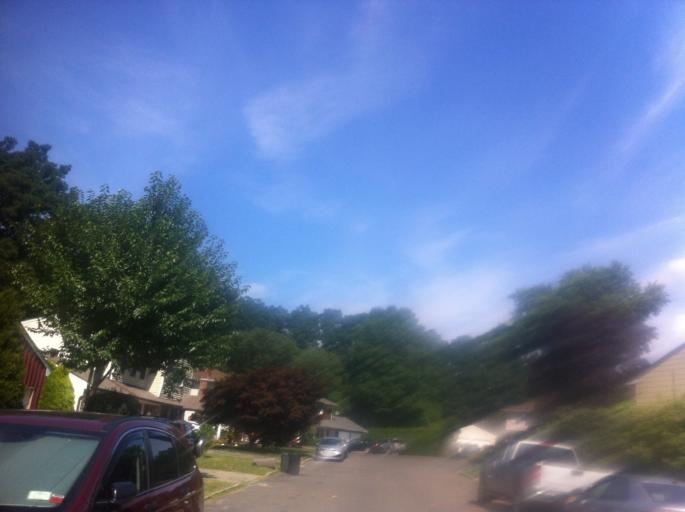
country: US
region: New York
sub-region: Nassau County
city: Locust Valley
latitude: 40.8603
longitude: -73.6120
